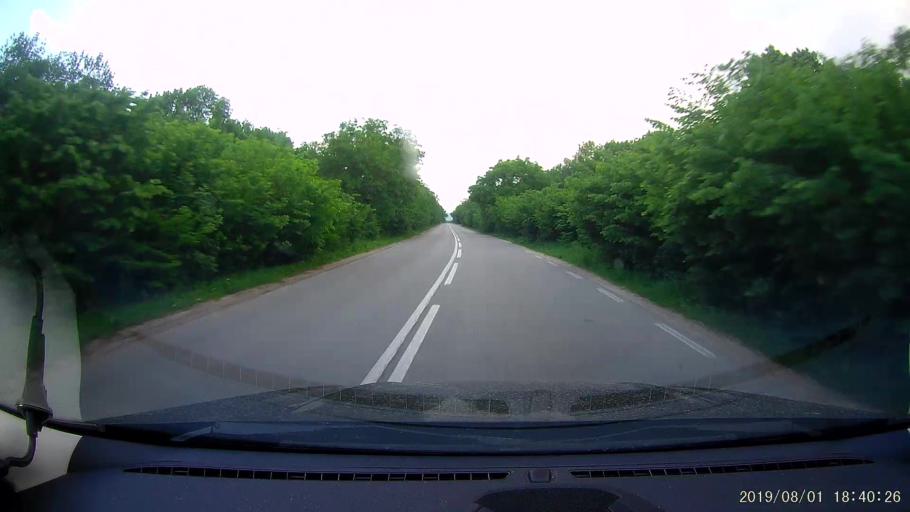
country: BG
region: Shumen
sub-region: Obshtina Khitrino
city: Gara Khitrino
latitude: 43.3671
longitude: 26.9193
